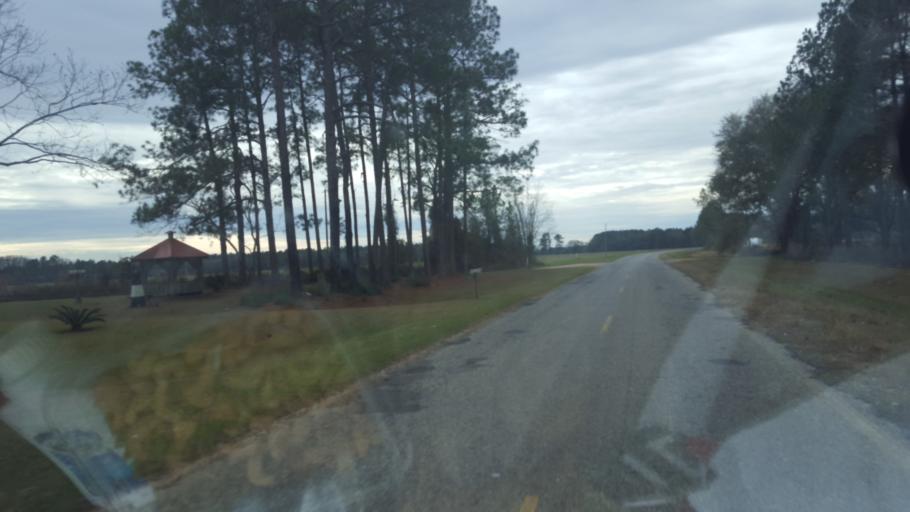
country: US
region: Georgia
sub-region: Berrien County
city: Enigma
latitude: 31.3392
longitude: -83.2731
